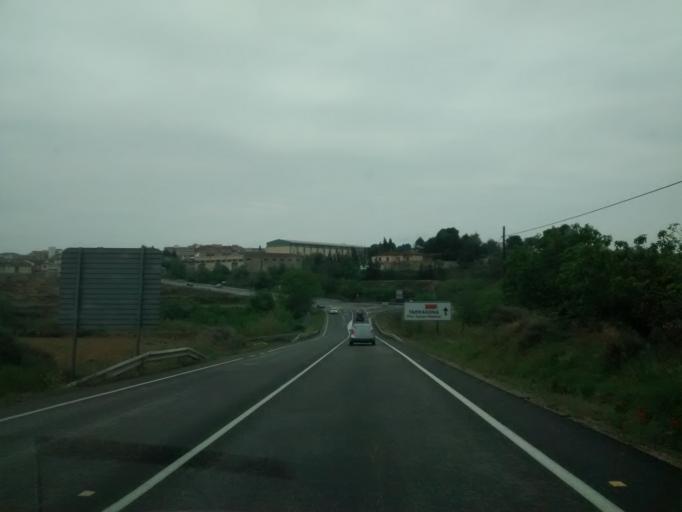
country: ES
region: Aragon
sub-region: Provincia de Zaragoza
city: Caspe
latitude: 41.2358
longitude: -0.0541
